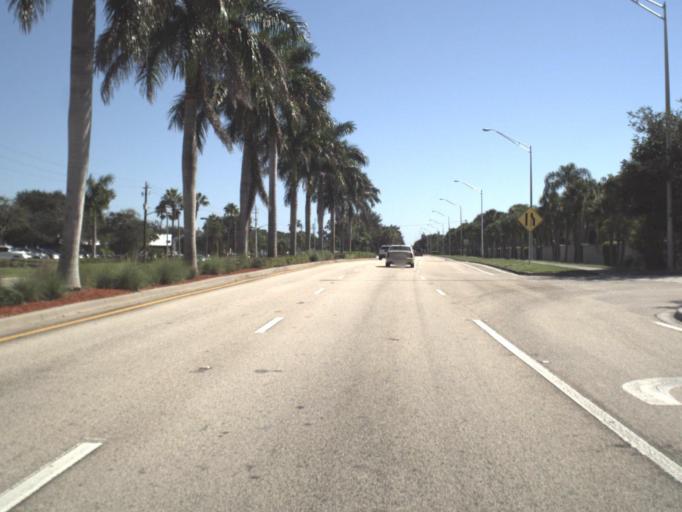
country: US
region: Florida
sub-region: Collier County
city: Naples
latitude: 26.1385
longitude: -81.7651
